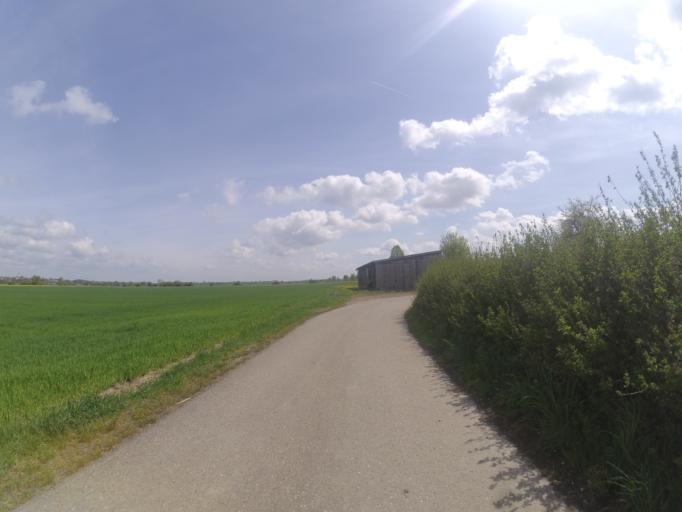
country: DE
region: Baden-Wuerttemberg
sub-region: Tuebingen Region
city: Griesingen
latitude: 48.2680
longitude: 9.7901
